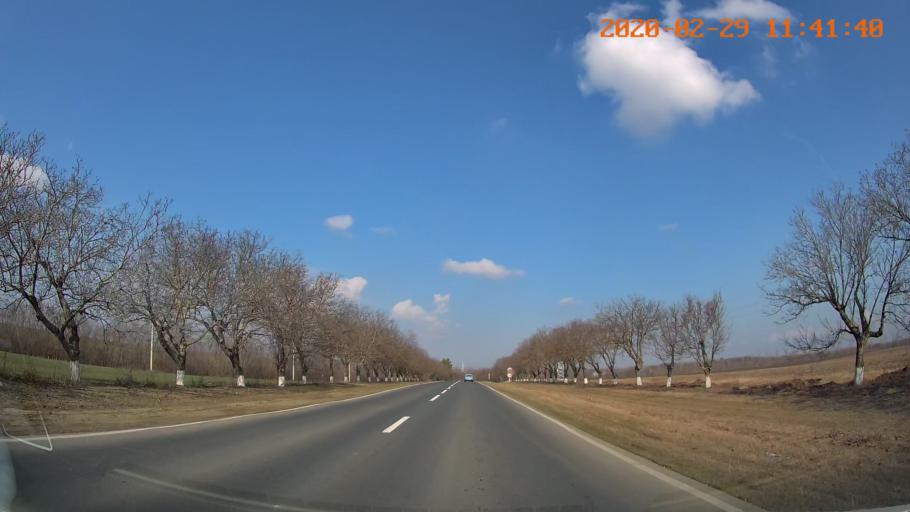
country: MD
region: Rezina
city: Saharna
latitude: 47.6748
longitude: 29.0156
